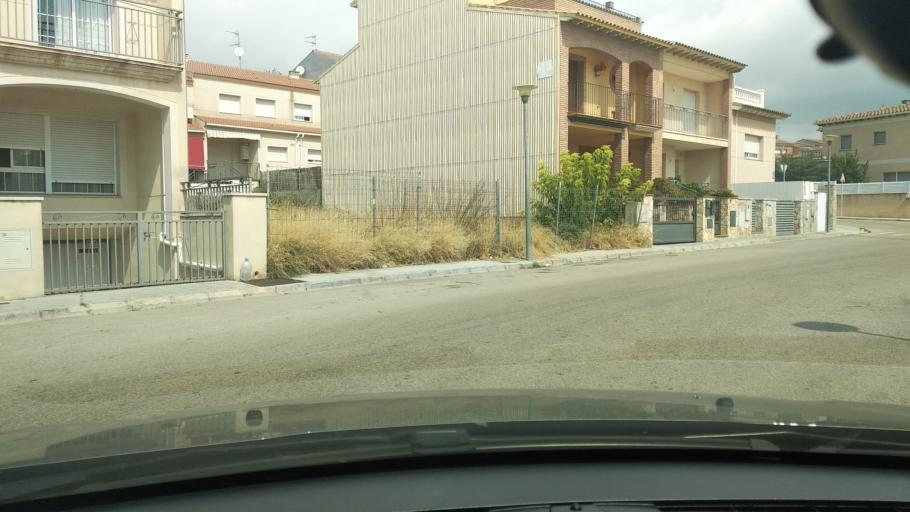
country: ES
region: Catalonia
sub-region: Provincia de Tarragona
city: El Vendrell
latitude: 41.2210
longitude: 1.5220
